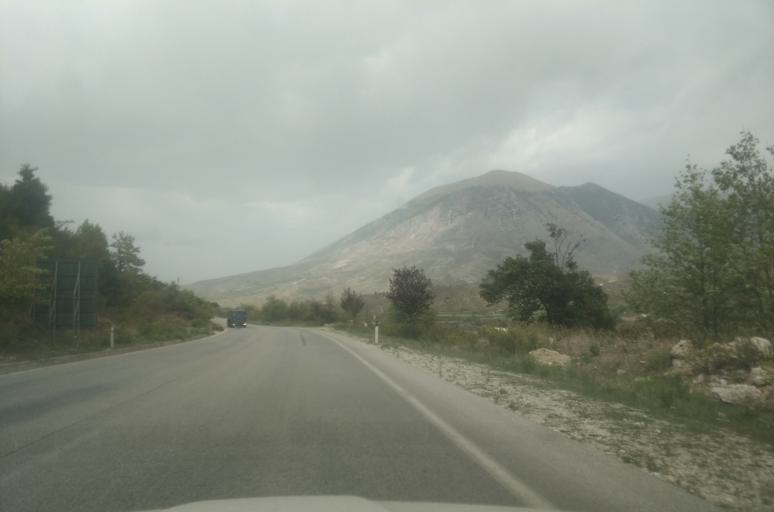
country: AL
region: Gjirokaster
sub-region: Rrethi i Tepelenes
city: Tepelene
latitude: 40.2615
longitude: 20.0524
